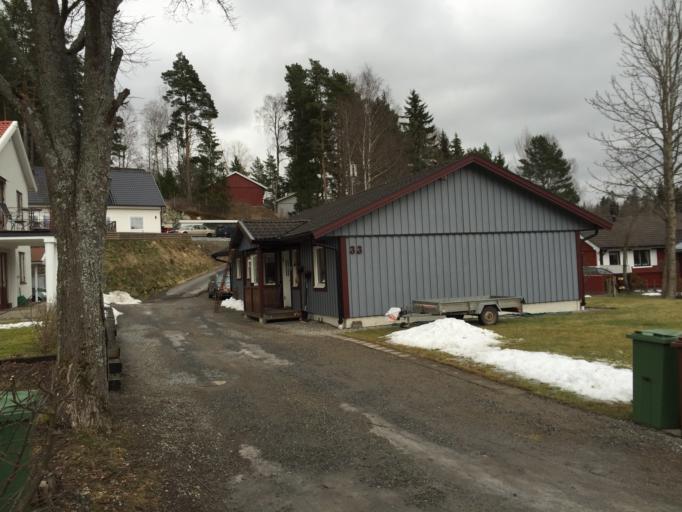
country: SE
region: Stockholm
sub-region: Salems Kommun
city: Ronninge
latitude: 59.2015
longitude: 17.7225
